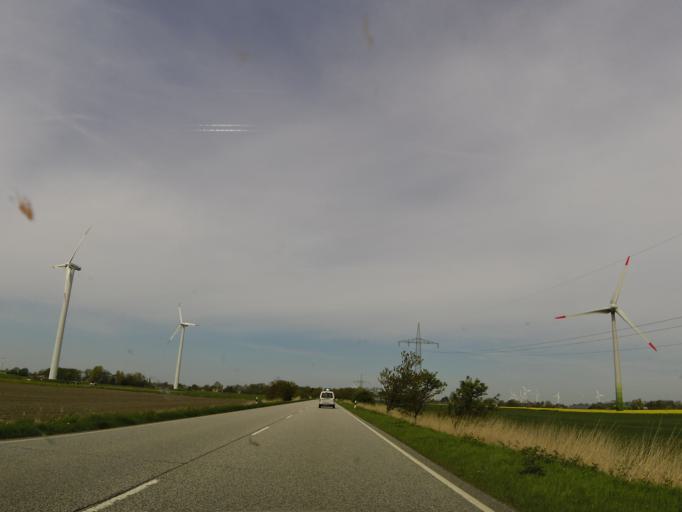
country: DE
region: Schleswig-Holstein
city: Hemme
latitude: 54.2699
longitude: 9.0195
